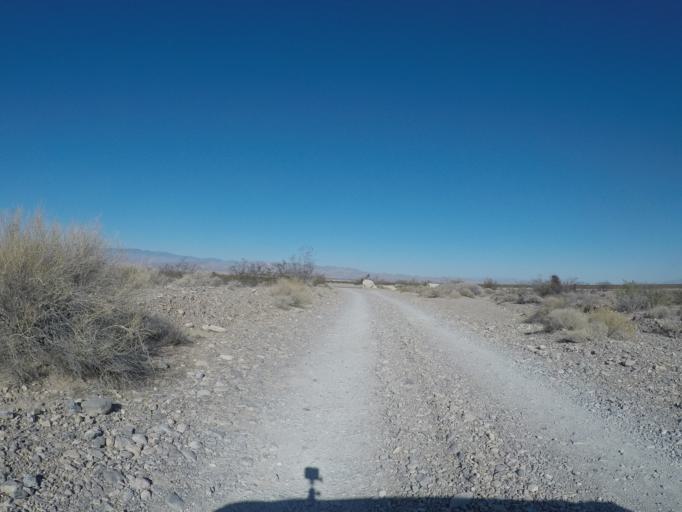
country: US
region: Nevada
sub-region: Clark County
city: Moapa Valley
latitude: 36.4473
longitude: -114.6771
